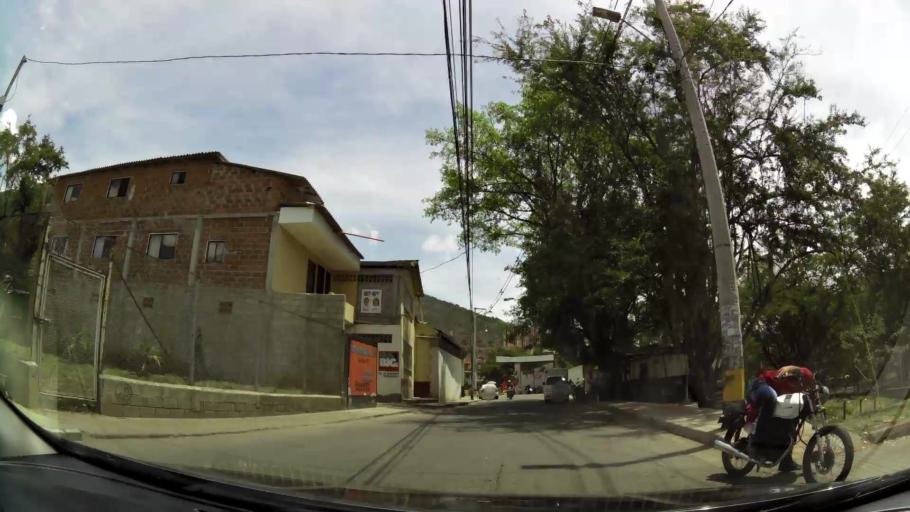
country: CO
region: Antioquia
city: Bello
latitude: 6.3485
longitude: -75.5655
